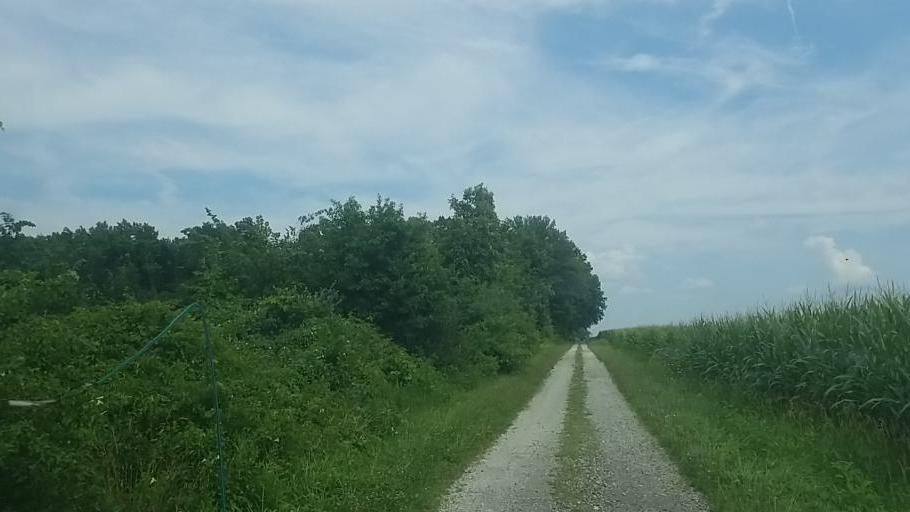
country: US
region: Ohio
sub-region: Hardin County
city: Forest
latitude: 40.7748
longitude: -83.5876
